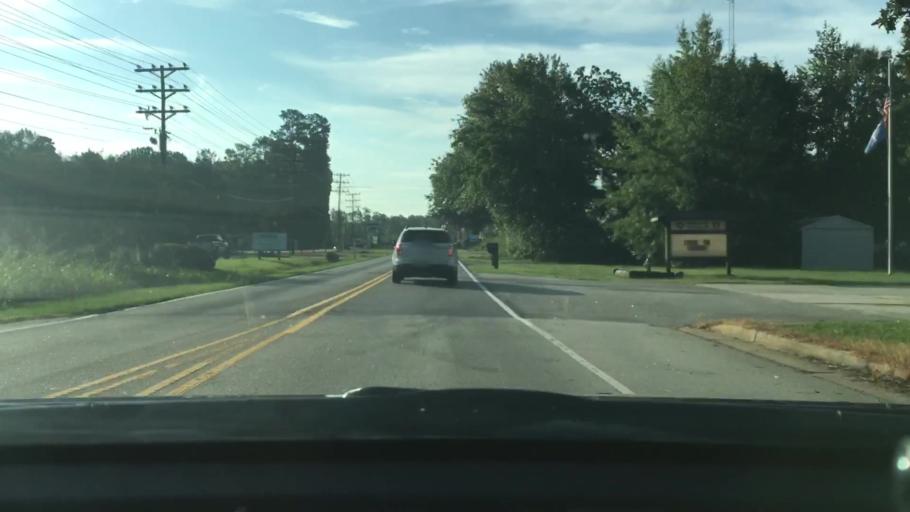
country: US
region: South Carolina
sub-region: Richland County
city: Lake Murray of Richland
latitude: 34.1258
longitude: -81.2162
